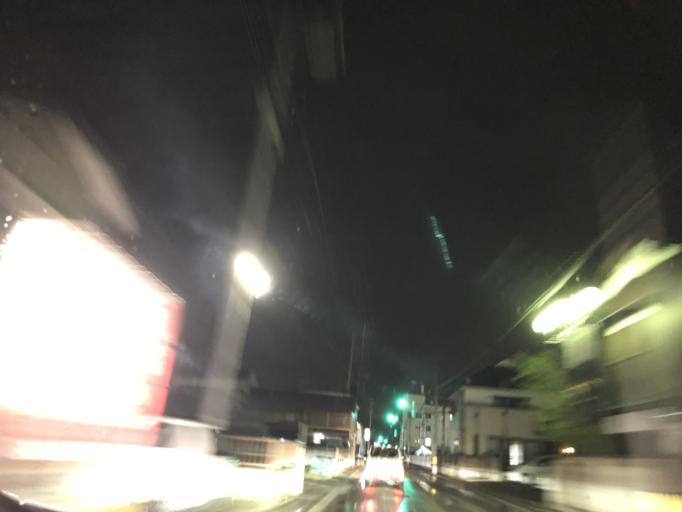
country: JP
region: Tochigi
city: Sano
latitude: 36.3121
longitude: 139.5707
